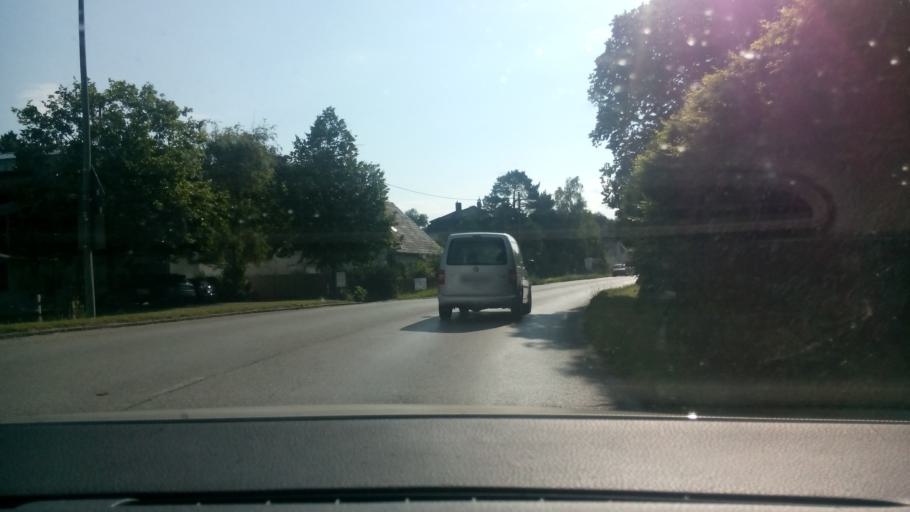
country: DE
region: Bavaria
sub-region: Upper Bavaria
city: Oberschleissheim
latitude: 48.2519
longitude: 11.5626
